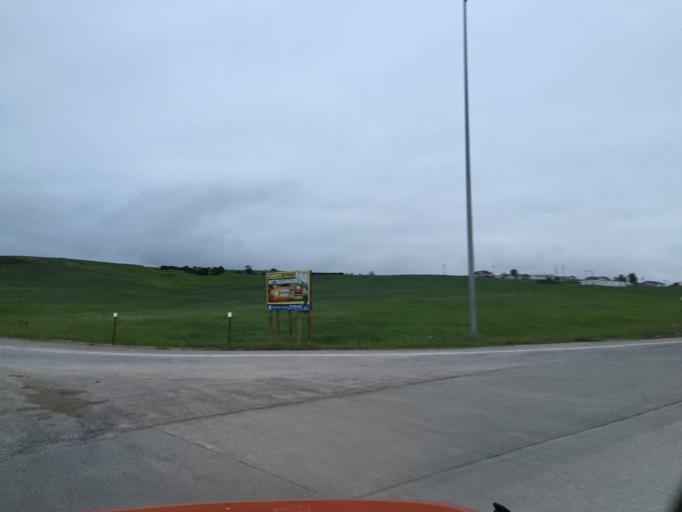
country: US
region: South Dakota
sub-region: Pennington County
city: Colonial Pine Hills
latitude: 43.8366
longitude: -103.1995
